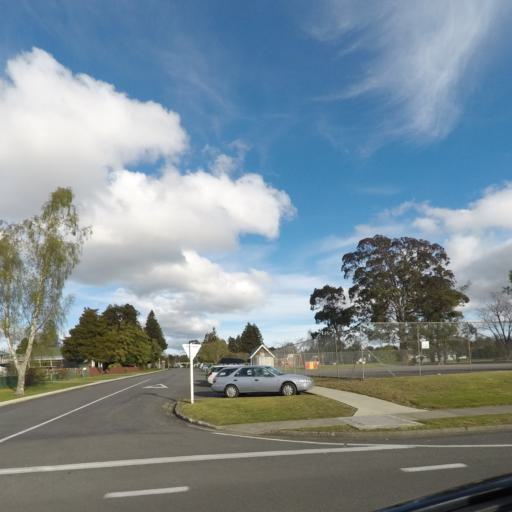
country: NZ
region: Manawatu-Wanganui
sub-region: Ruapehu District
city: Waiouru
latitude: -39.4153
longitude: 175.4013
